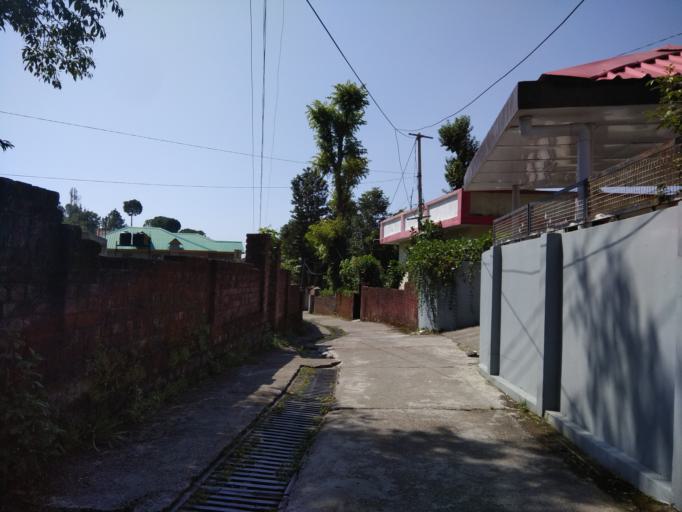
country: IN
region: Himachal Pradesh
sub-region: Kangra
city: Palampur
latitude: 32.1220
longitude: 76.5396
